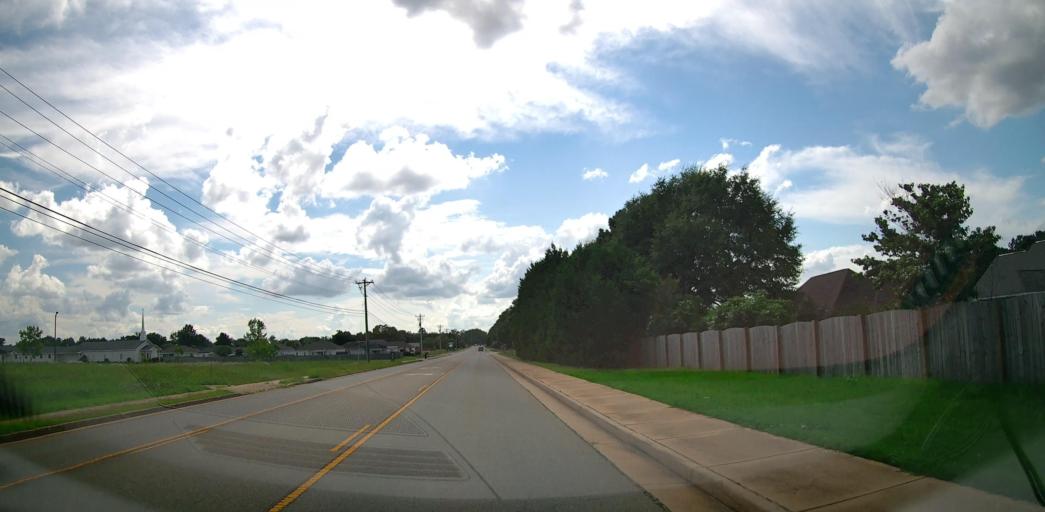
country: US
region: Georgia
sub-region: Houston County
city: Centerville
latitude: 32.5710
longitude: -83.6843
